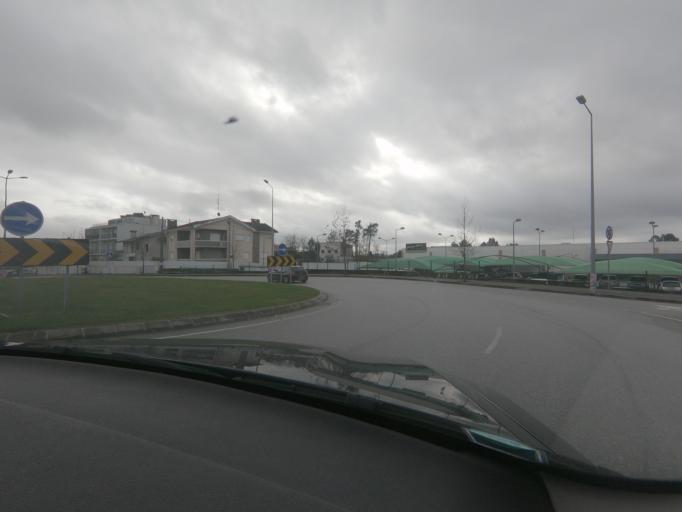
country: PT
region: Viseu
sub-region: Viseu
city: Abraveses
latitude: 40.6857
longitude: -7.9278
